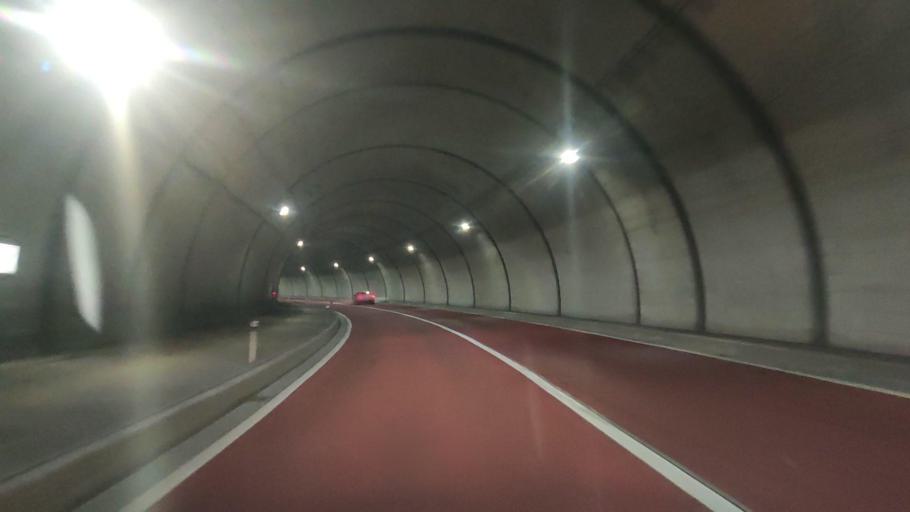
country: JP
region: Oita
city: Oita
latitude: 33.0917
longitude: 131.6486
